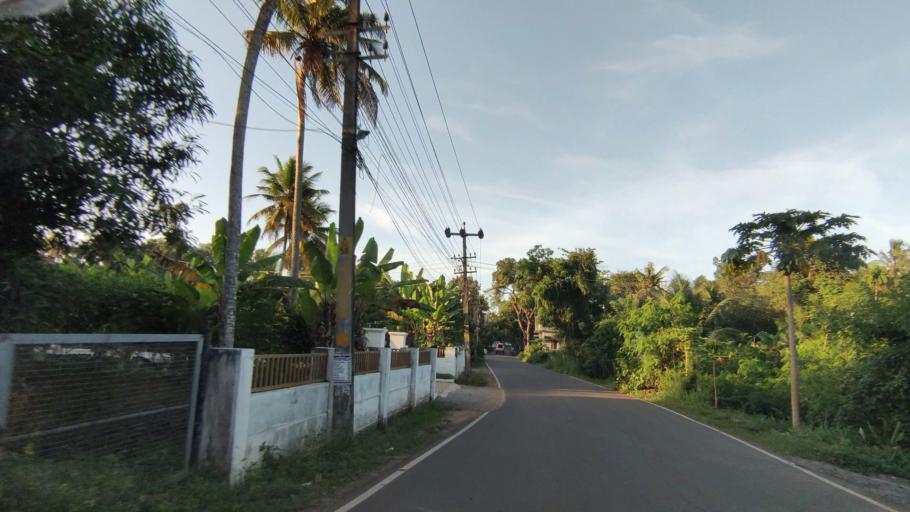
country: IN
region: Kerala
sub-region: Kottayam
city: Kottayam
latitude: 9.6194
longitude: 76.4938
